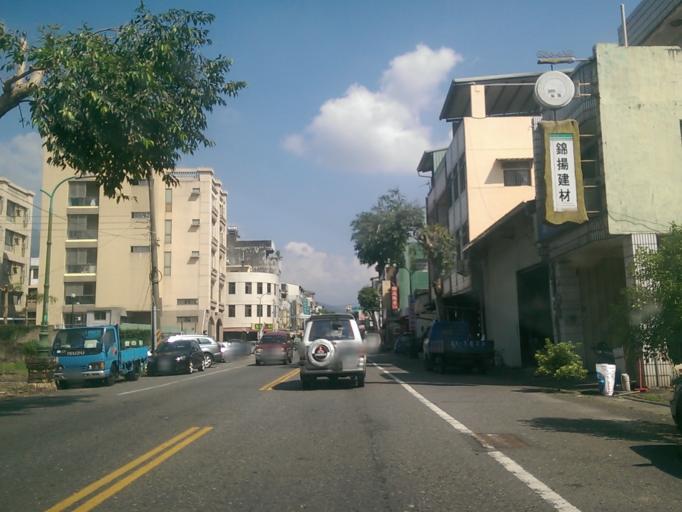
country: TW
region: Taiwan
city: Lugu
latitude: 23.8268
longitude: 120.7807
